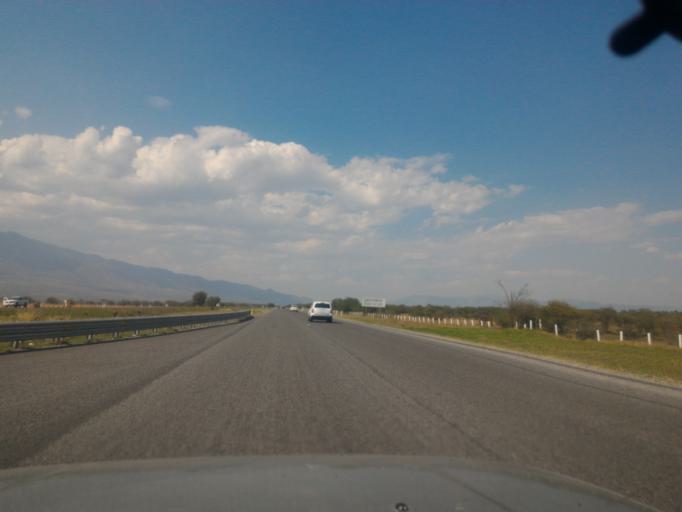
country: MX
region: Jalisco
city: Atoyac
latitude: 19.9759
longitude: -103.5352
